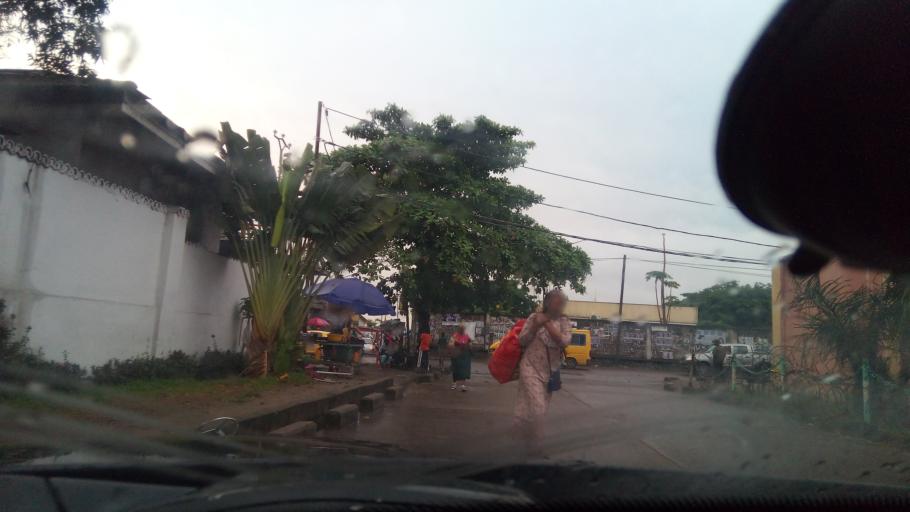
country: CD
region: Kinshasa
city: Kinshasa
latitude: -4.3451
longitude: 15.2402
